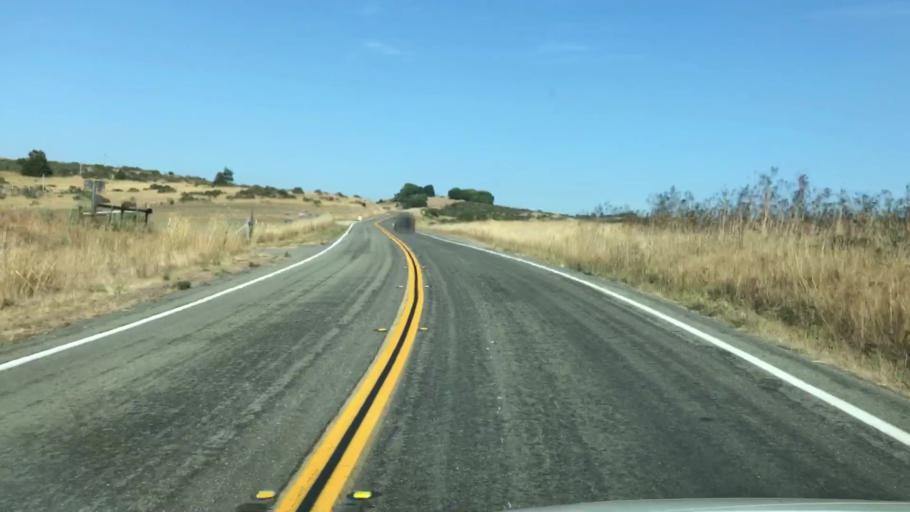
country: US
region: California
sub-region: Marin County
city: Inverness
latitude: 38.0437
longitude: -122.7821
